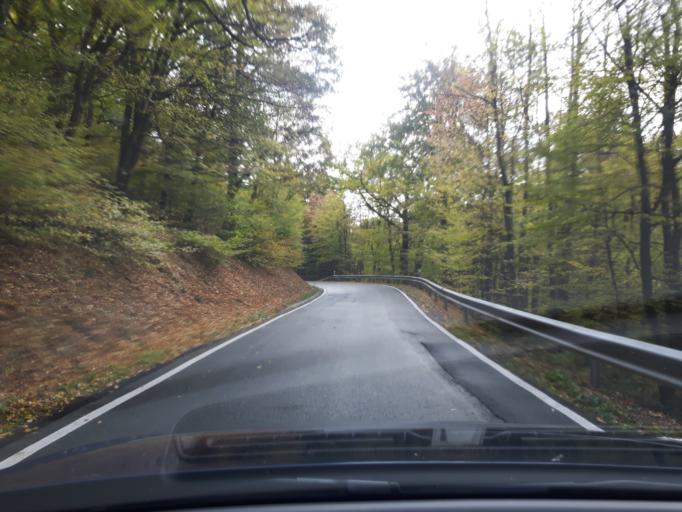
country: DE
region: North Rhine-Westphalia
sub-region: Regierungsbezirk Arnsberg
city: Bad Berleburg
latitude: 51.0182
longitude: 8.4244
